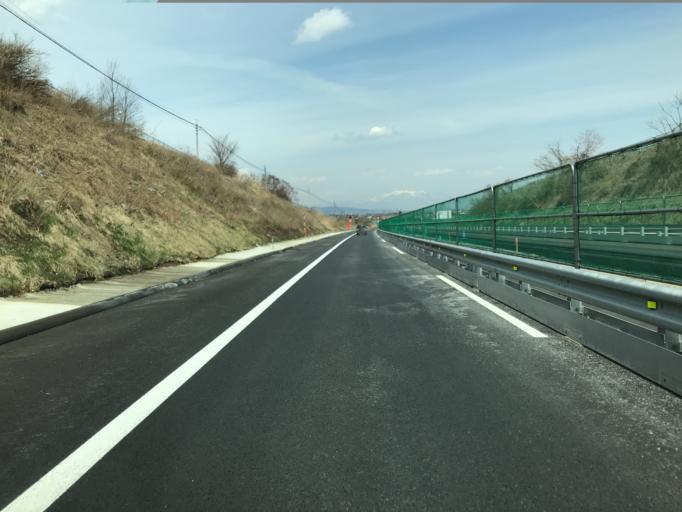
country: JP
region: Yamagata
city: Kaminoyama
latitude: 38.1952
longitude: 140.2985
